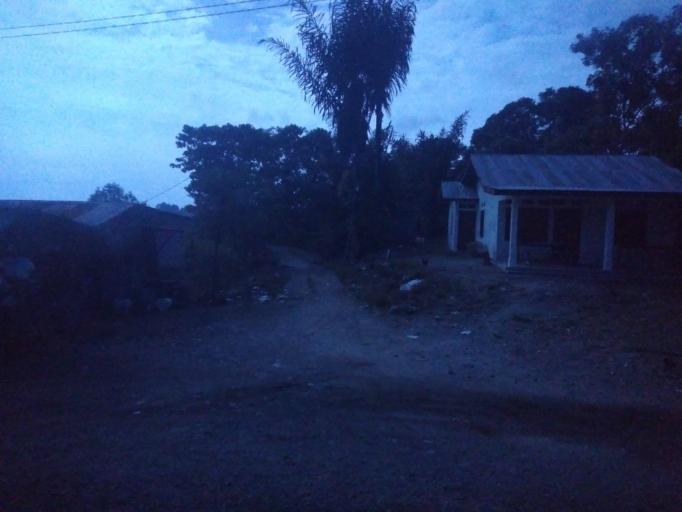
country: ID
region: North Sumatra
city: Parapat
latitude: 2.7483
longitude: 98.9709
